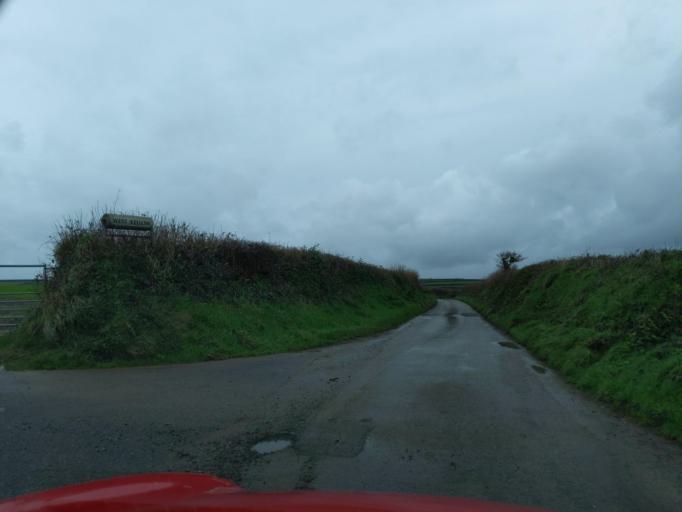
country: GB
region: England
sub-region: Cornwall
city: Duloe
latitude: 50.3462
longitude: -4.5336
